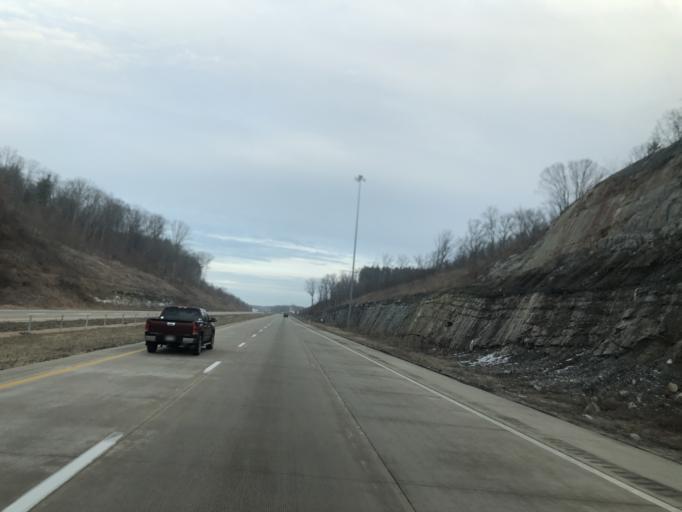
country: US
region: Ohio
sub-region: Athens County
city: Nelsonville
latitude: 39.4480
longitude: -82.2086
